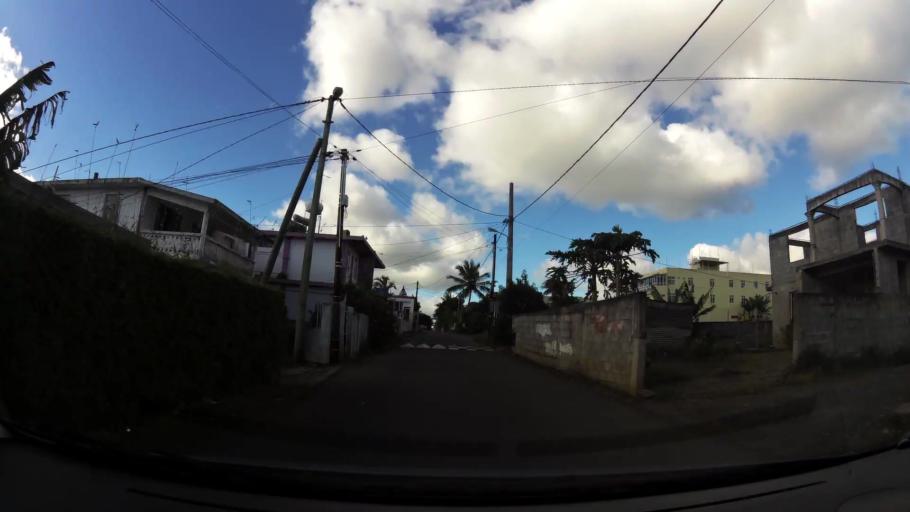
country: MU
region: Plaines Wilhems
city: Vacoas
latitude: -20.2919
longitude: 57.4872
